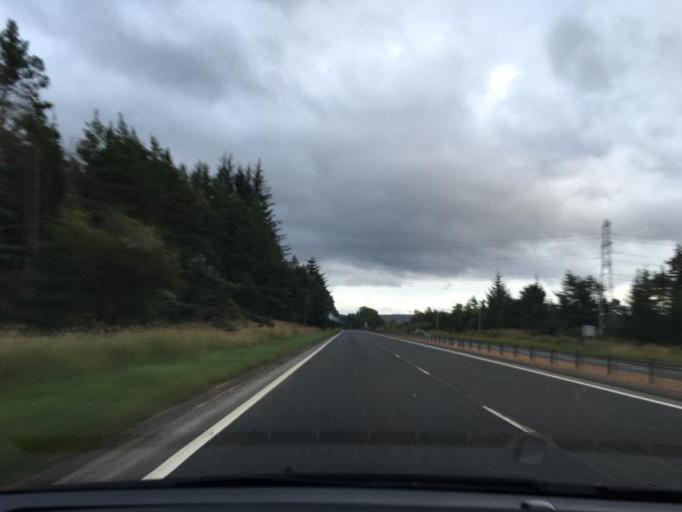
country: GB
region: Scotland
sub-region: Highland
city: Inverness
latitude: 57.4403
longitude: -4.1438
